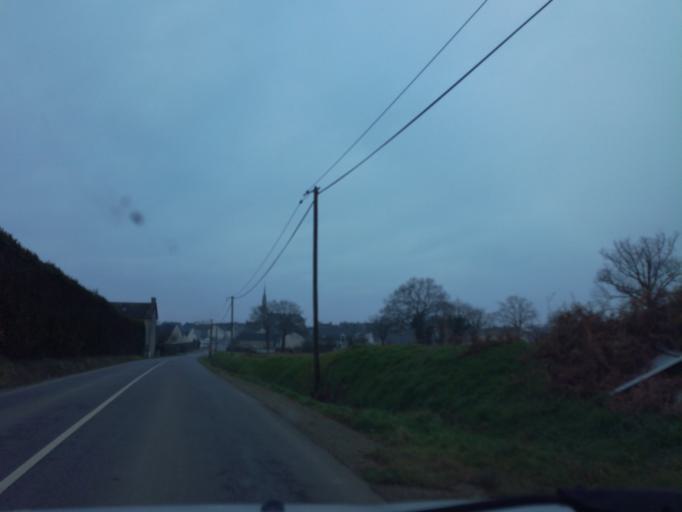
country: FR
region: Brittany
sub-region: Departement d'Ille-et-Vilaine
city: Gosne
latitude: 48.2492
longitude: -1.4599
